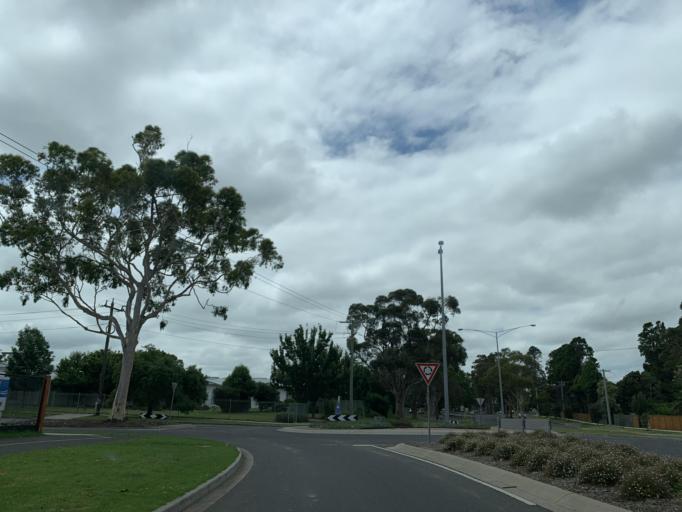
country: AU
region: Victoria
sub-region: Wellington
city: Sale
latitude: -38.1114
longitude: 147.0812
